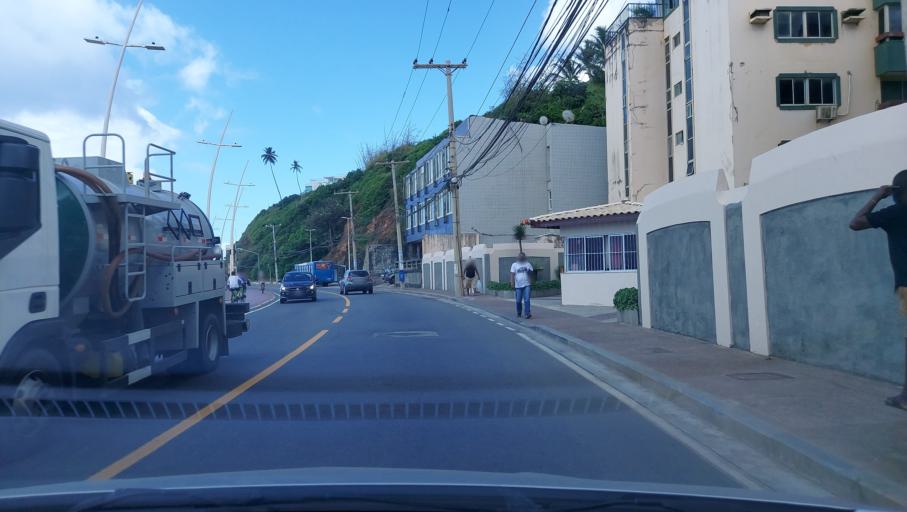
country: BR
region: Bahia
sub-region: Salvador
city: Salvador
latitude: -13.0103
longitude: -38.5026
